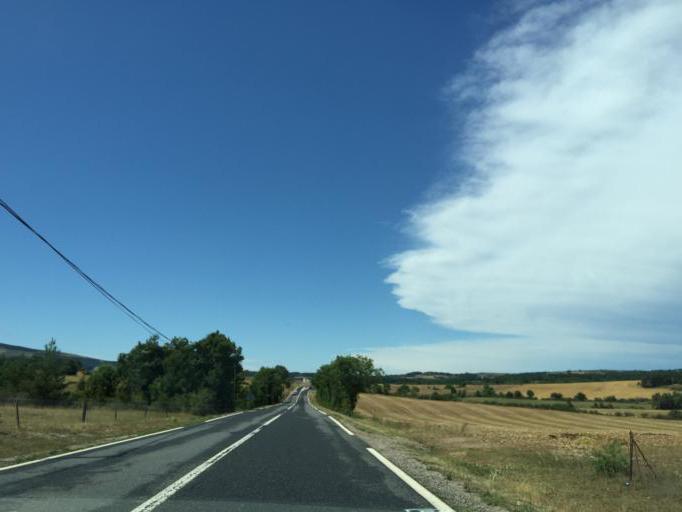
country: FR
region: Midi-Pyrenees
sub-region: Departement de l'Aveyron
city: Severac-le-Chateau
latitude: 44.2186
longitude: 3.0014
